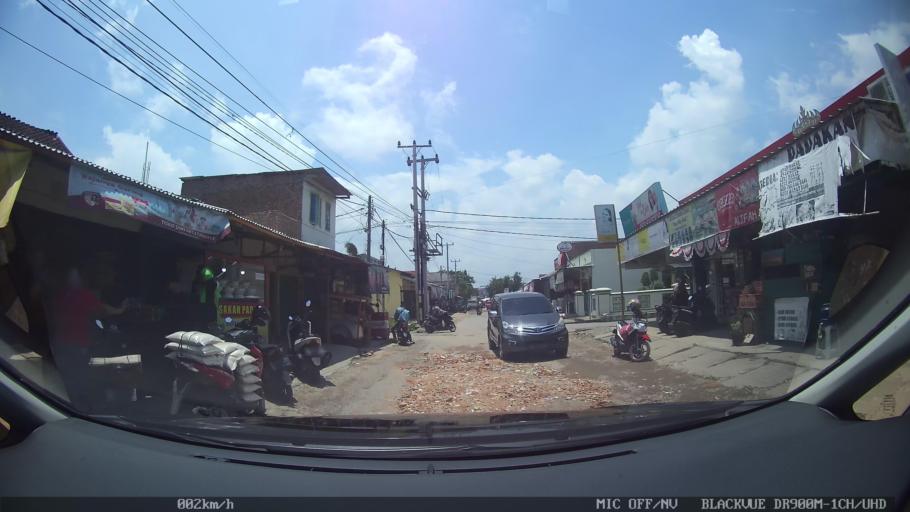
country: ID
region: Lampung
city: Kedaton
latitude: -5.3831
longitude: 105.2920
